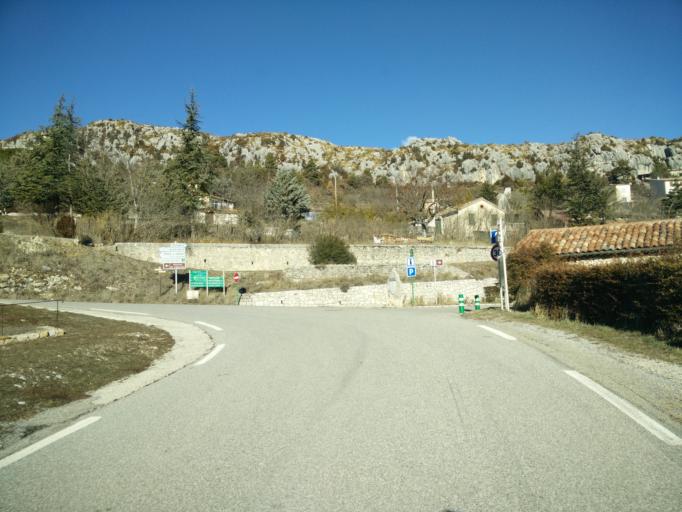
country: FR
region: Provence-Alpes-Cote d'Azur
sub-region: Departement des Alpes-de-Haute-Provence
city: Castellane
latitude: 43.7601
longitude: 6.4417
